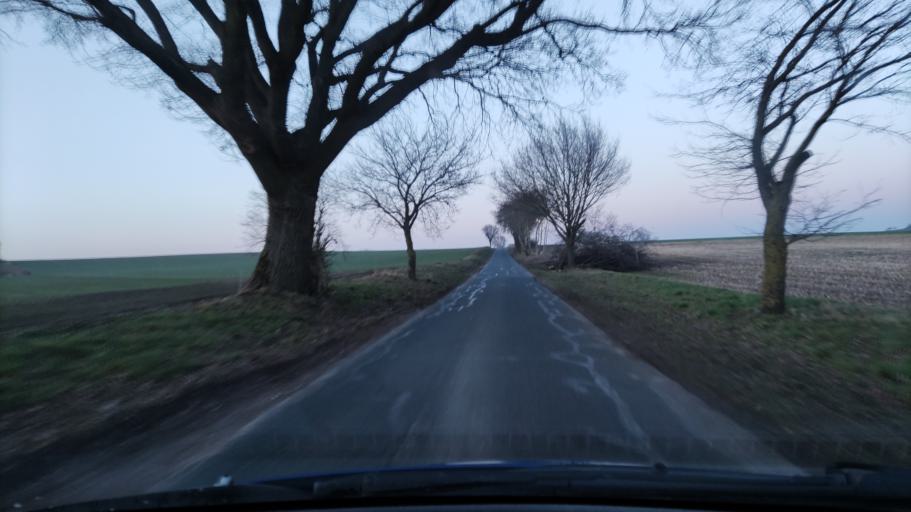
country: DE
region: Lower Saxony
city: Natendorf
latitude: 53.0484
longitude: 10.4782
